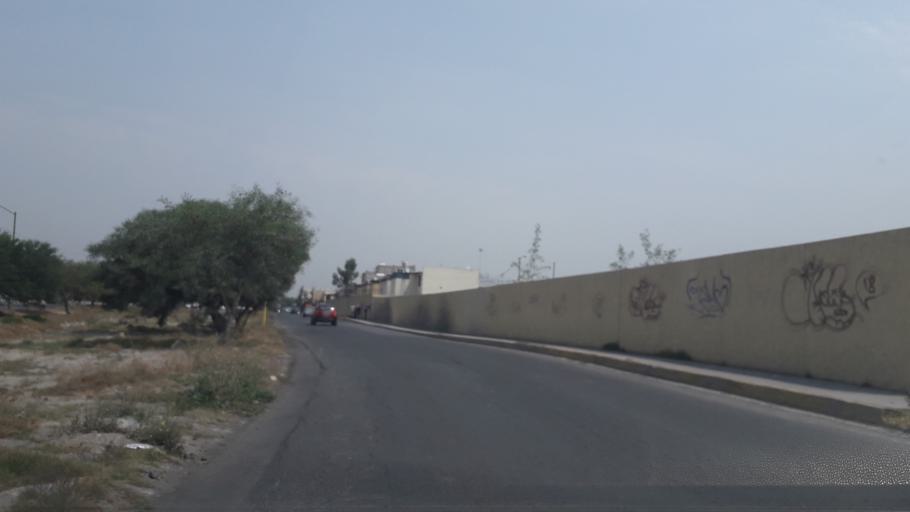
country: MX
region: Mexico
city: Santo Tomas Chiconautla
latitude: 19.6416
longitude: -99.0231
